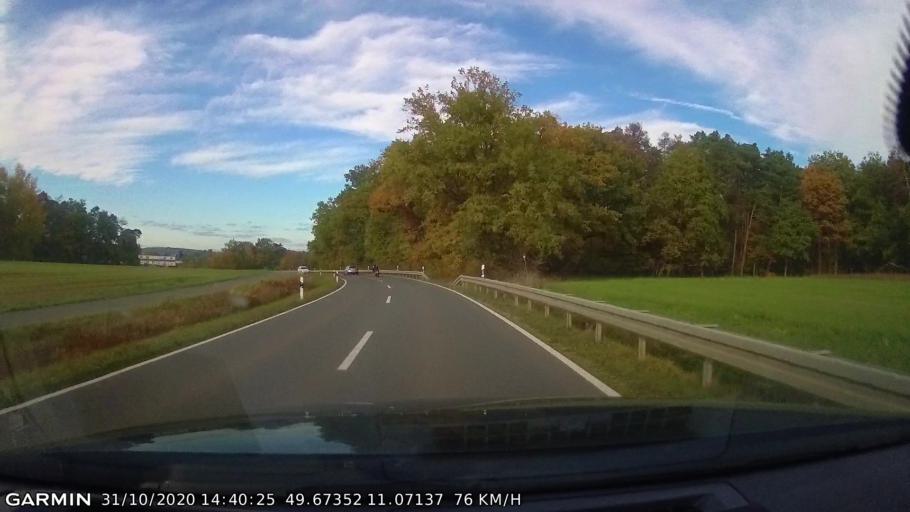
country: DE
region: Bavaria
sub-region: Upper Franconia
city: Poxdorf
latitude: 49.6736
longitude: 11.0709
